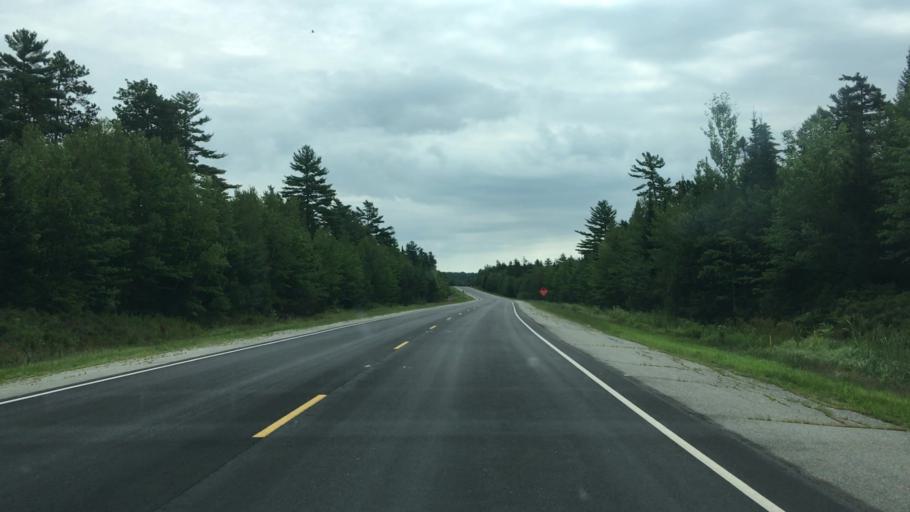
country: US
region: Maine
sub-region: Washington County
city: Addison
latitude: 44.9064
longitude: -67.8254
